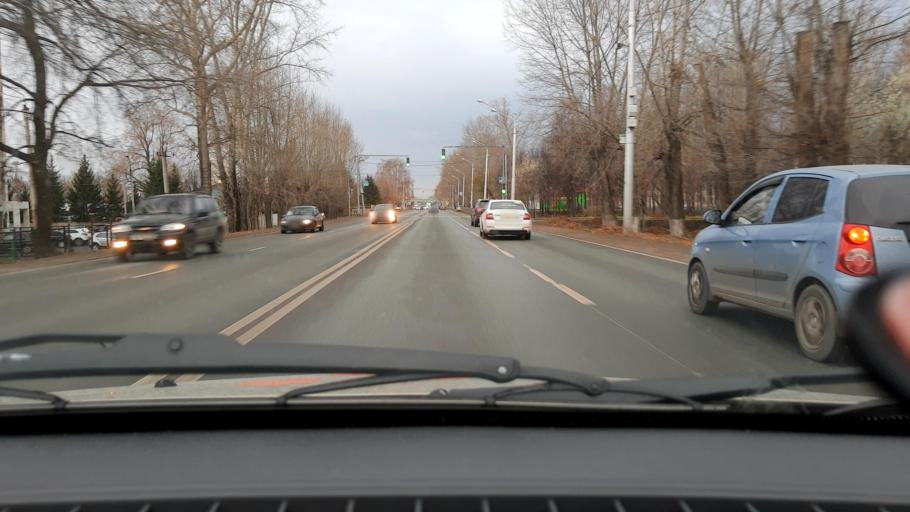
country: RU
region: Bashkortostan
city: Mikhaylovka
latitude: 54.7020
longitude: 55.8427
